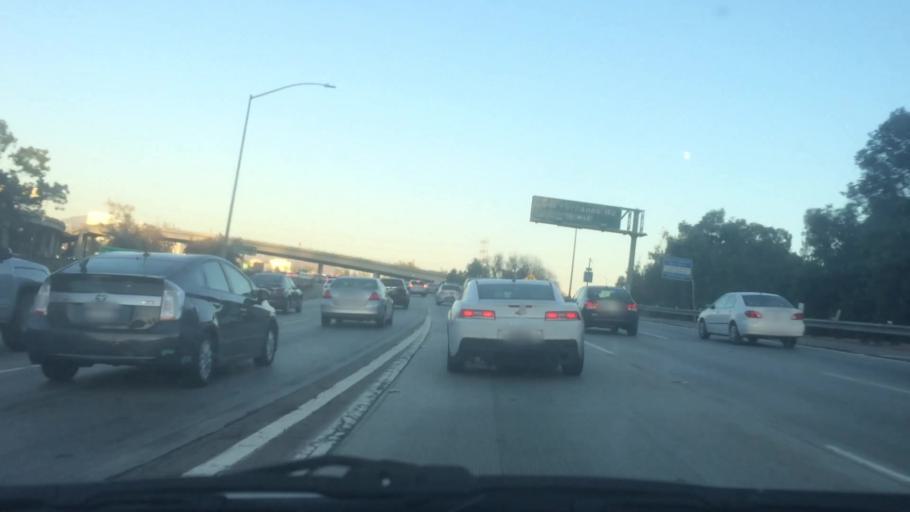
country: US
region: California
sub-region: Los Angeles County
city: North Glendale
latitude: 34.1517
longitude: -118.2787
